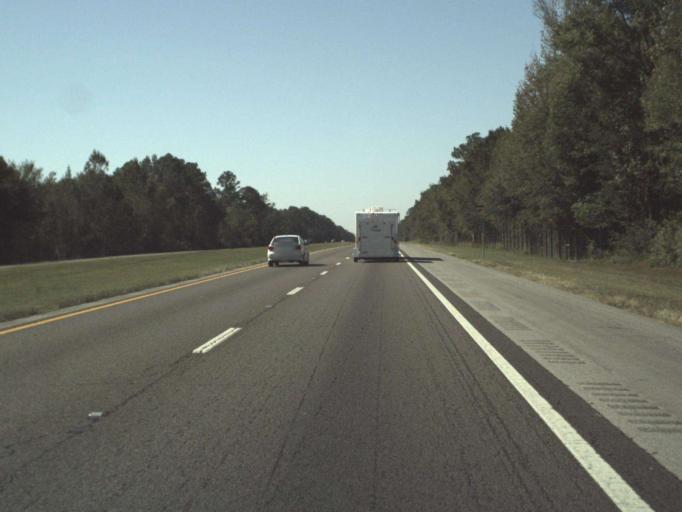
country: US
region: Florida
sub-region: Santa Rosa County
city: East Milton
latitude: 30.6360
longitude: -86.9197
